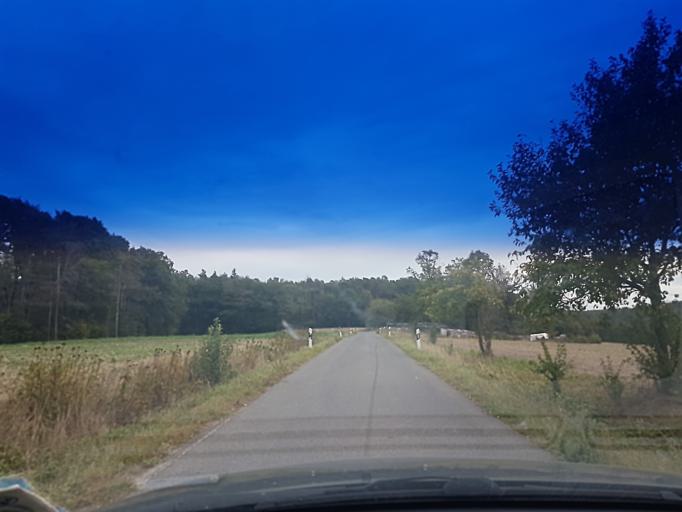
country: DE
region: Bavaria
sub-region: Regierungsbezirk Unterfranken
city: Geiselwind
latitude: 49.8227
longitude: 10.4920
